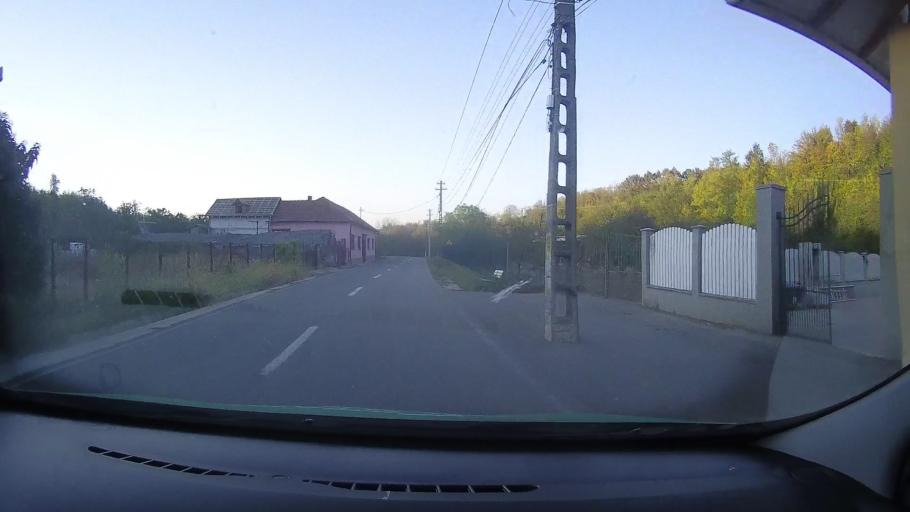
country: RO
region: Timis
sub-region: Comuna Traian Vuia
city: Traian Vuia
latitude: 45.7617
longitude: 22.0978
